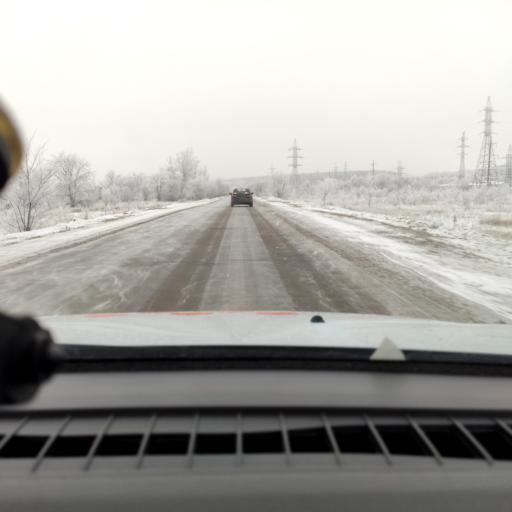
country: RU
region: Samara
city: Samara
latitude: 53.1092
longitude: 50.2257
